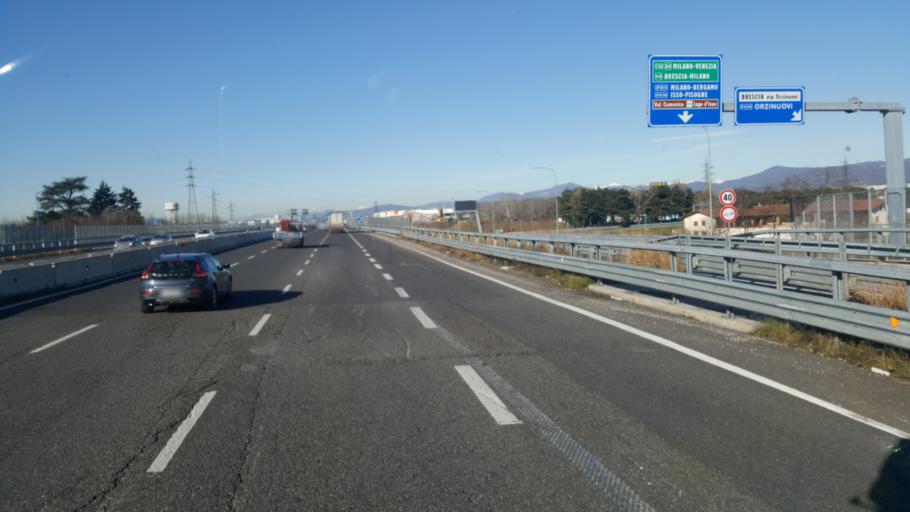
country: IT
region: Lombardy
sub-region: Provincia di Brescia
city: Roncadelle
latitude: 45.5277
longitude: 10.1718
